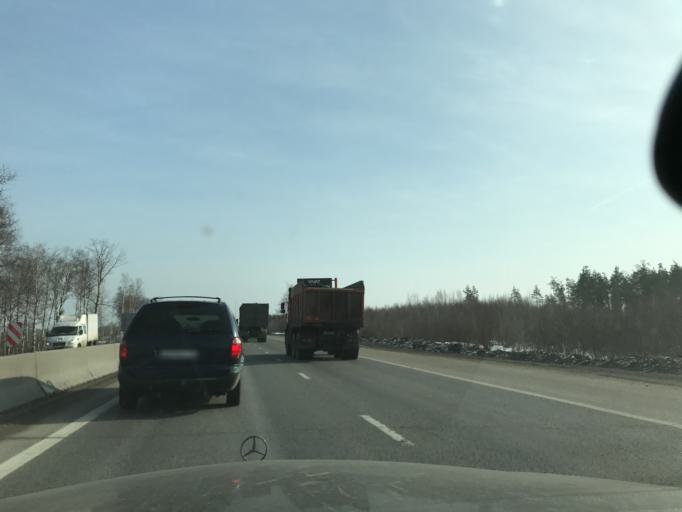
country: RU
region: Nizjnij Novgorod
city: Babino
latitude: 56.3035
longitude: 43.6009
